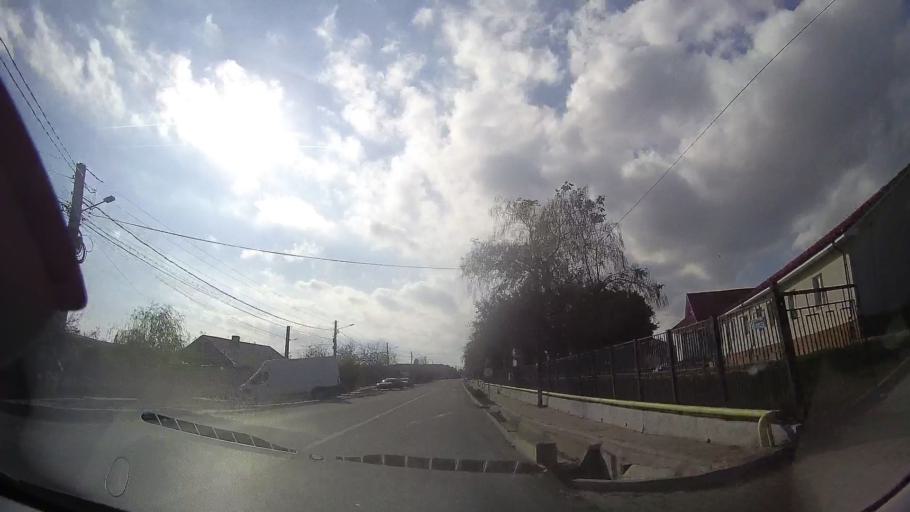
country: RO
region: Constanta
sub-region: Comuna Douazeci si Trei August
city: Dulcesti
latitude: 43.9073
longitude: 28.5482
